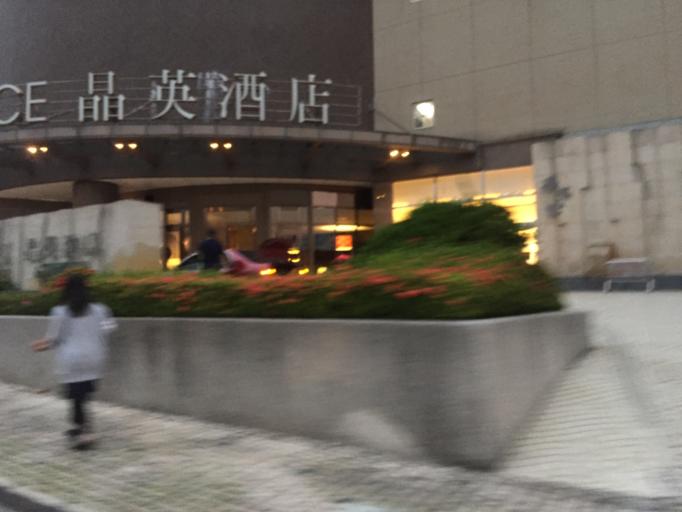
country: TW
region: Taiwan
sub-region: Yilan
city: Yilan
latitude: 24.7535
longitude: 121.7505
